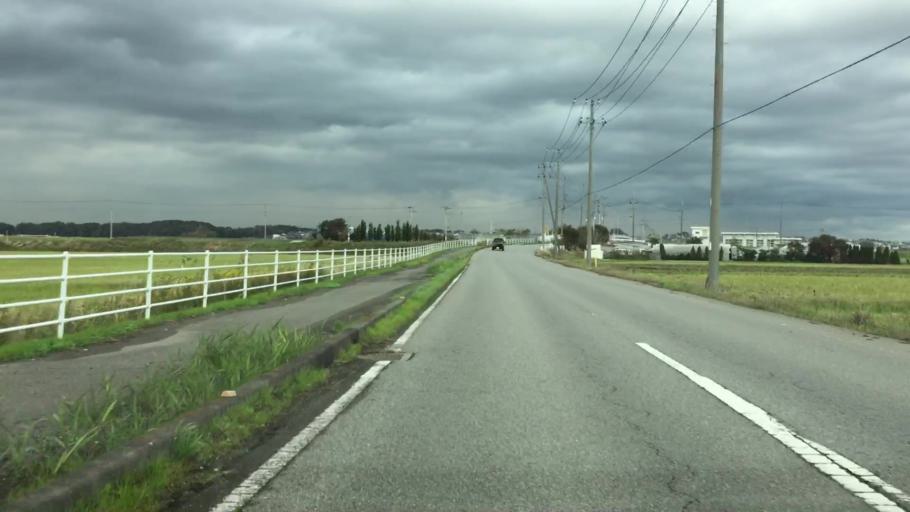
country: JP
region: Chiba
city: Shiroi
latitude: 35.8450
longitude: 140.0970
